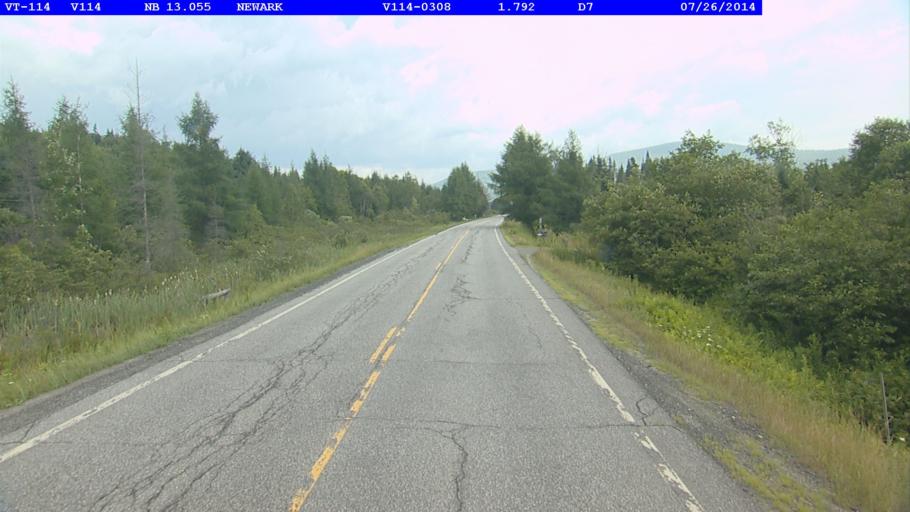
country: US
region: Vermont
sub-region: Caledonia County
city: Lyndonville
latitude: 44.6937
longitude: -71.8733
